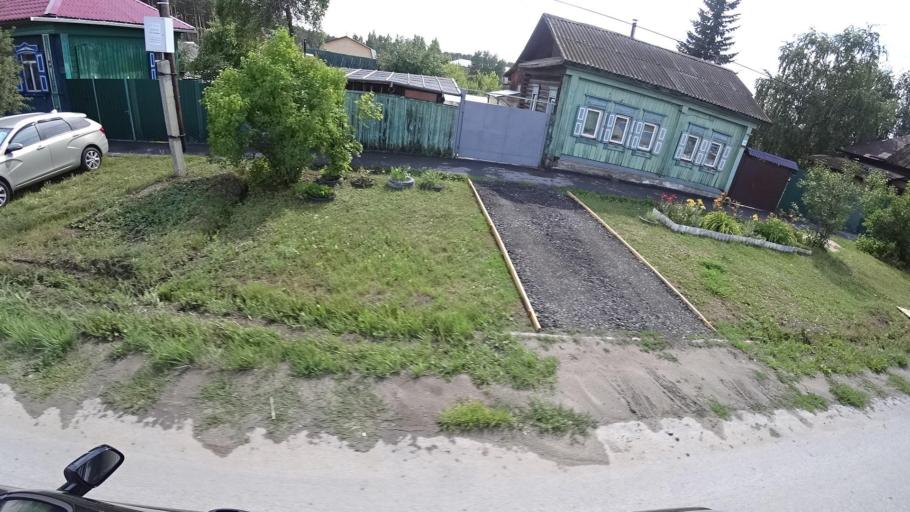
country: RU
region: Sverdlovsk
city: Kamyshlov
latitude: 56.8370
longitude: 62.7358
